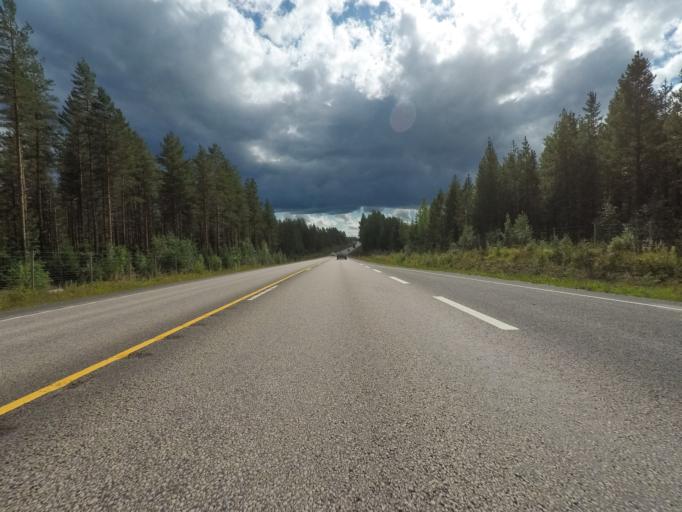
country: FI
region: Central Finland
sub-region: Jyvaeskylae
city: Toivakka
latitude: 61.9983
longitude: 26.0557
